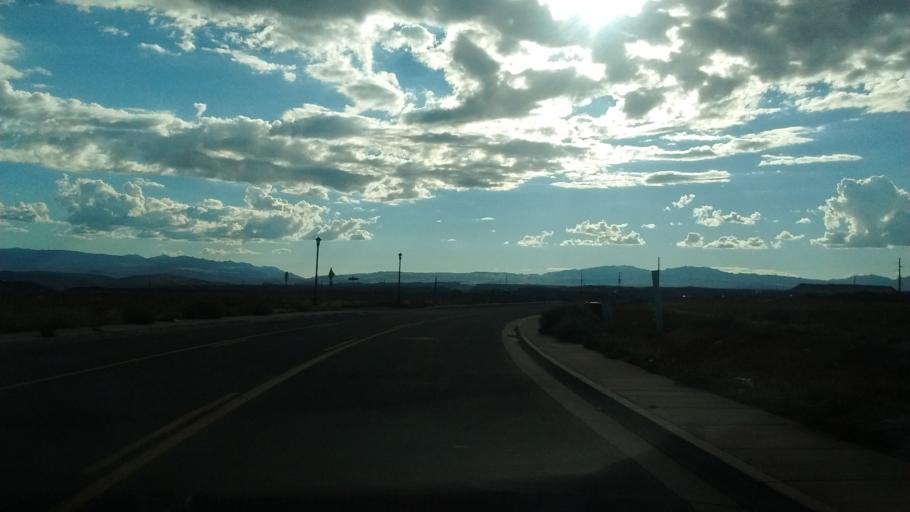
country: US
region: Utah
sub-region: Washington County
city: Washington
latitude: 37.1449
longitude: -113.4885
